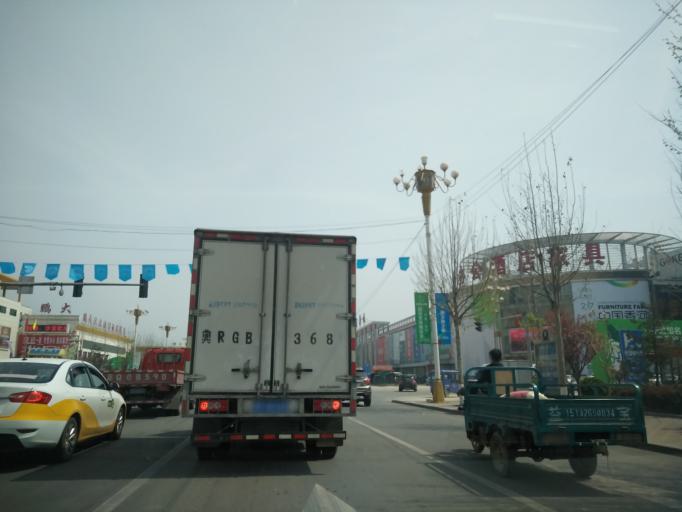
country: CN
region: Tianjin Shi
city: Xiawuqi
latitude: 39.7494
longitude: 117.0153
